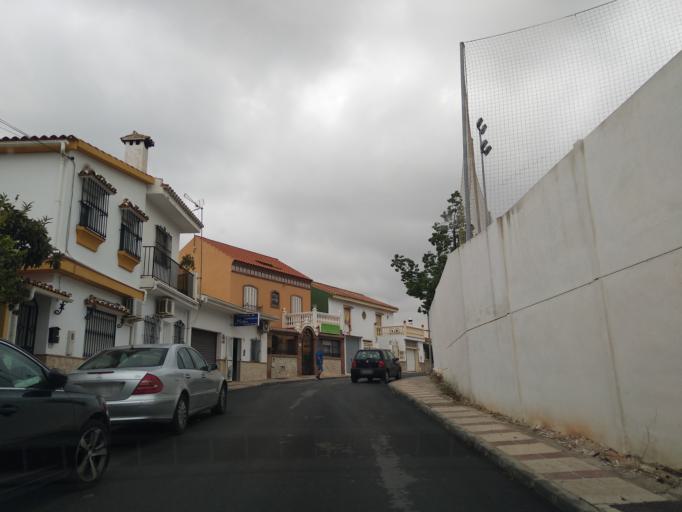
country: ES
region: Andalusia
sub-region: Provincia de Malaga
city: Malaga
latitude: 36.7411
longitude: -4.4794
